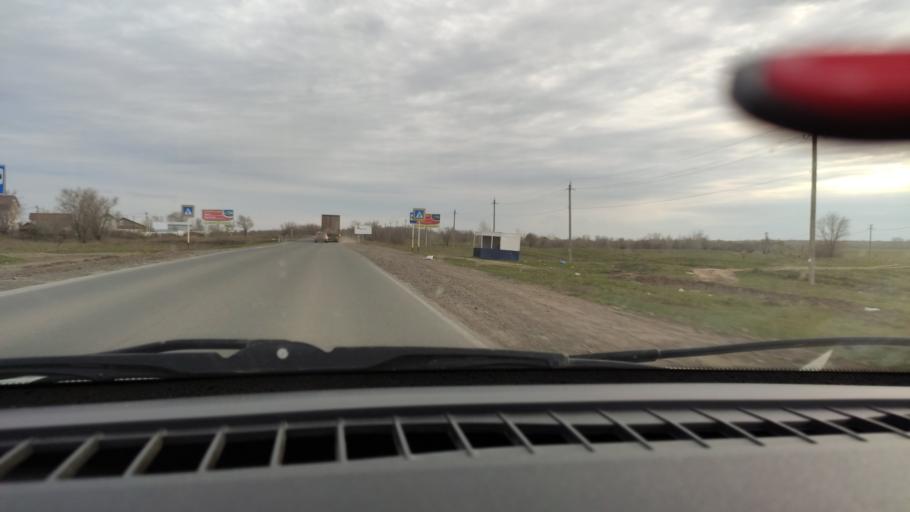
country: RU
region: Orenburg
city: Tatarskaya Kargala
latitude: 51.8992
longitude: 55.1646
